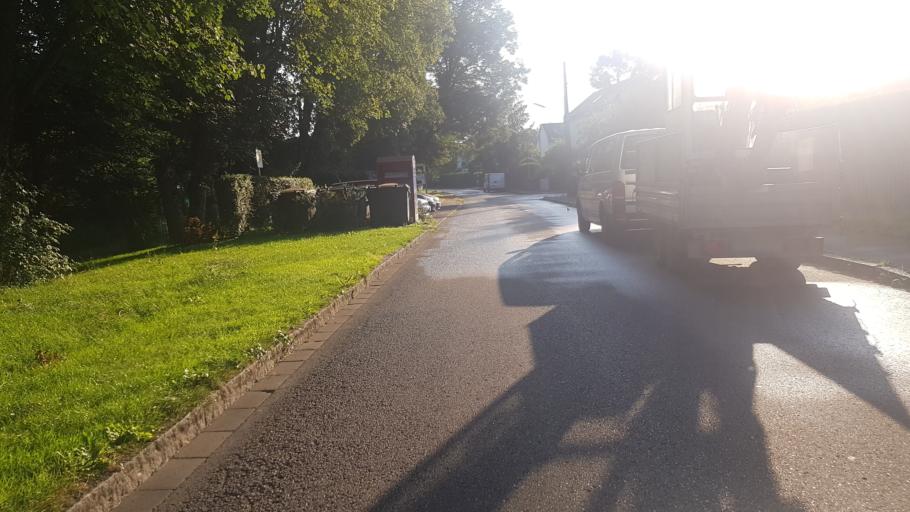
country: DE
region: Bavaria
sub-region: Upper Bavaria
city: Grafelfing
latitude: 48.1140
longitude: 11.4323
